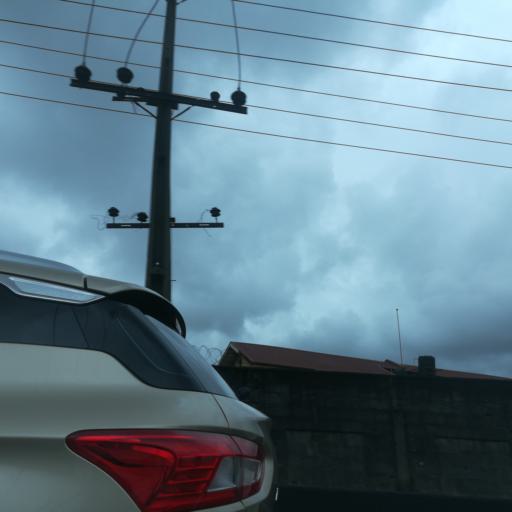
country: NG
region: Lagos
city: Lagos
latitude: 6.4577
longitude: 3.4066
